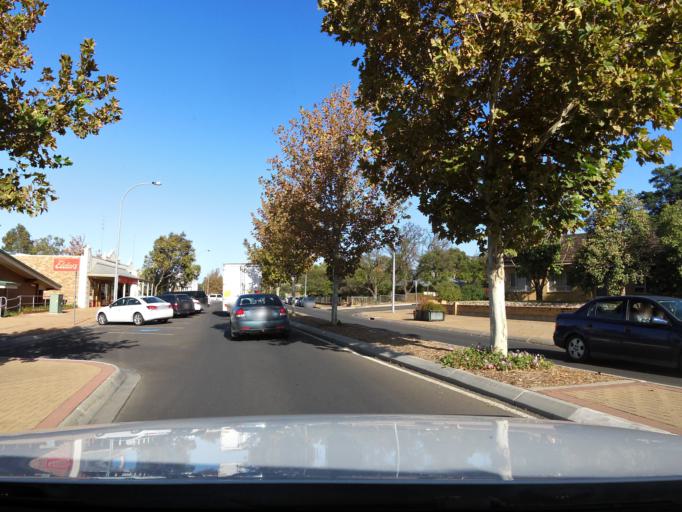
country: AU
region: South Australia
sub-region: Berri and Barmera
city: Berri
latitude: -34.2828
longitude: 140.6055
